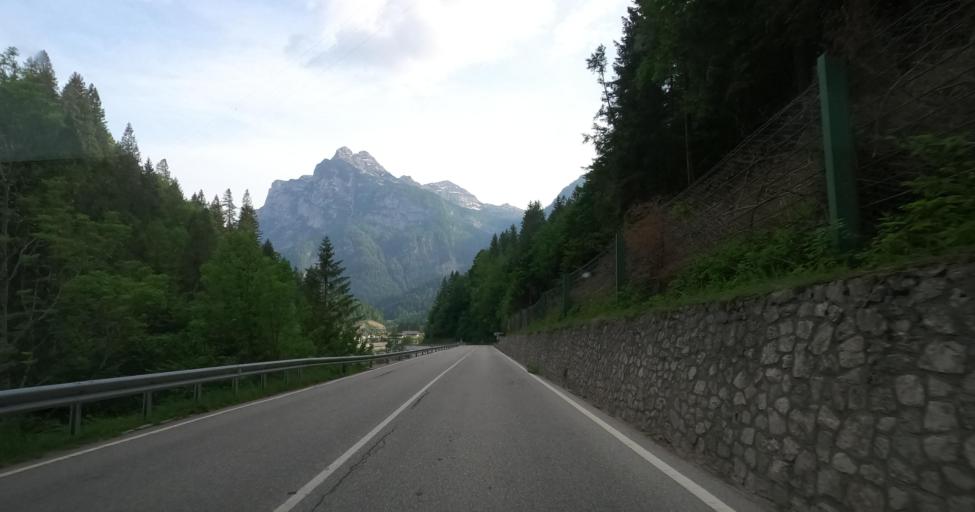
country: IT
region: Veneto
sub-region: Provincia di Belluno
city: Cencenighe Agordino
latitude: 46.3576
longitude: 11.9714
